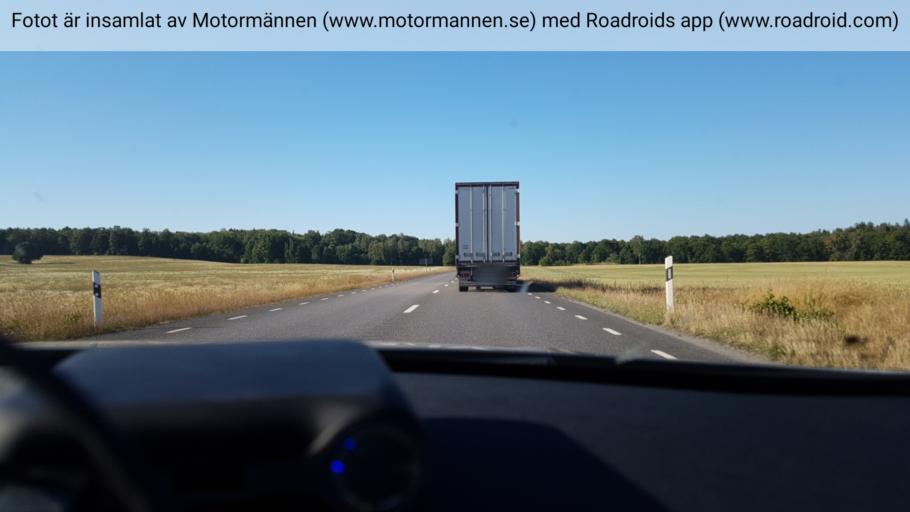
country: SE
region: Joenkoeping
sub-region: Habo Kommun
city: Habo
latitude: 57.9345
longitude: 14.0969
